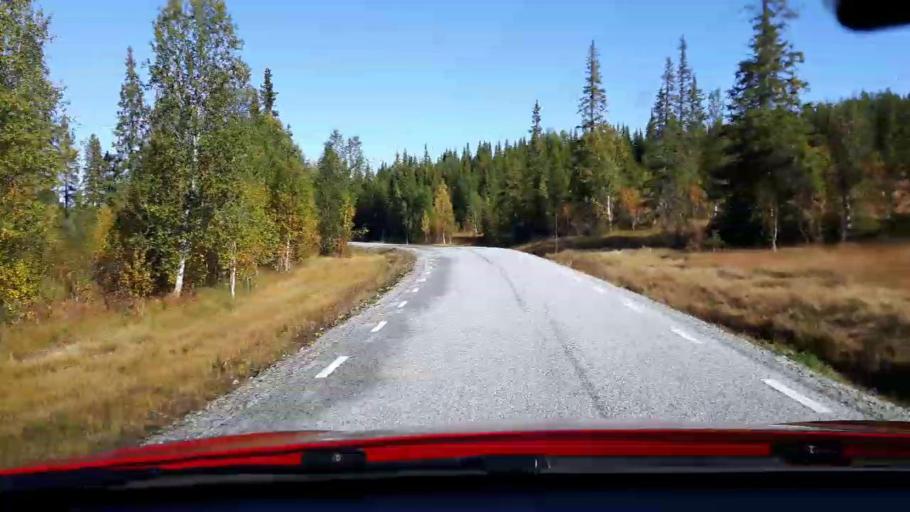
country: NO
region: Nord-Trondelag
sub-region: Lierne
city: Sandvika
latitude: 64.6167
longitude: 13.7009
